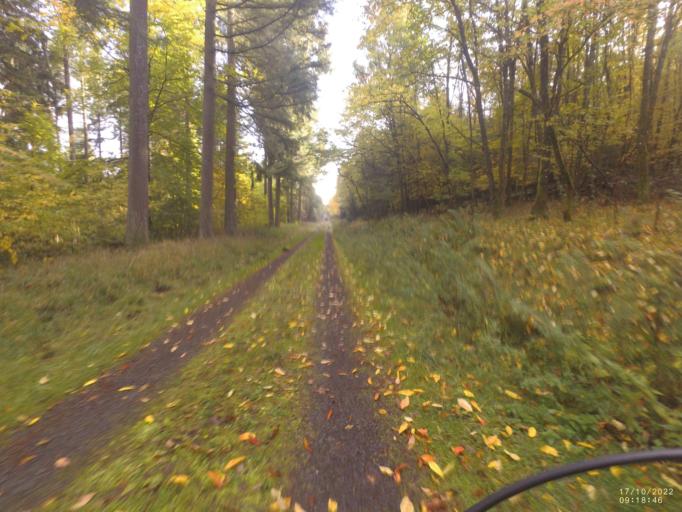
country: DE
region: Rheinland-Pfalz
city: Daun
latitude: 50.1950
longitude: 6.8530
